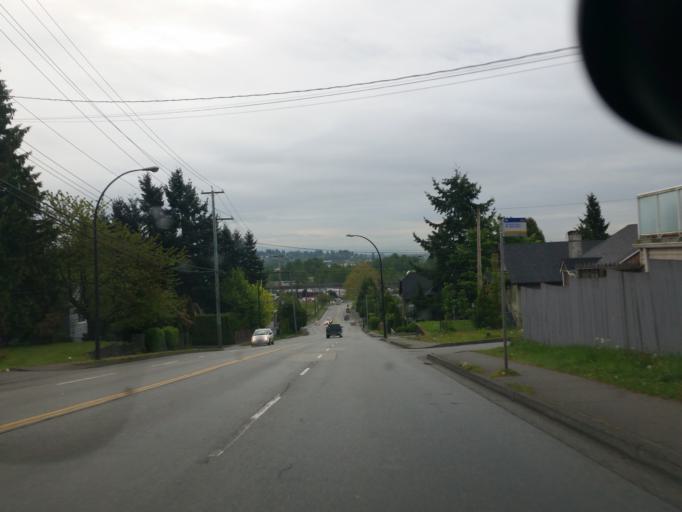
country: CA
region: British Columbia
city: New Westminster
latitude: 49.2315
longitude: -122.8900
